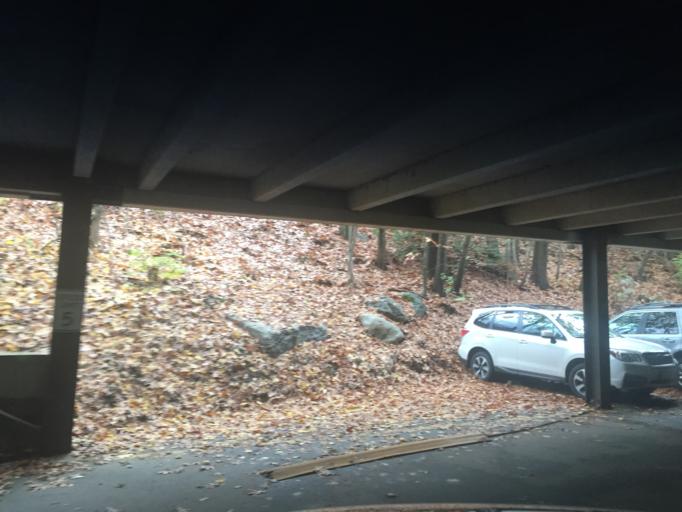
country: US
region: Massachusetts
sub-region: Norfolk County
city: Needham
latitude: 42.3145
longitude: -71.2486
